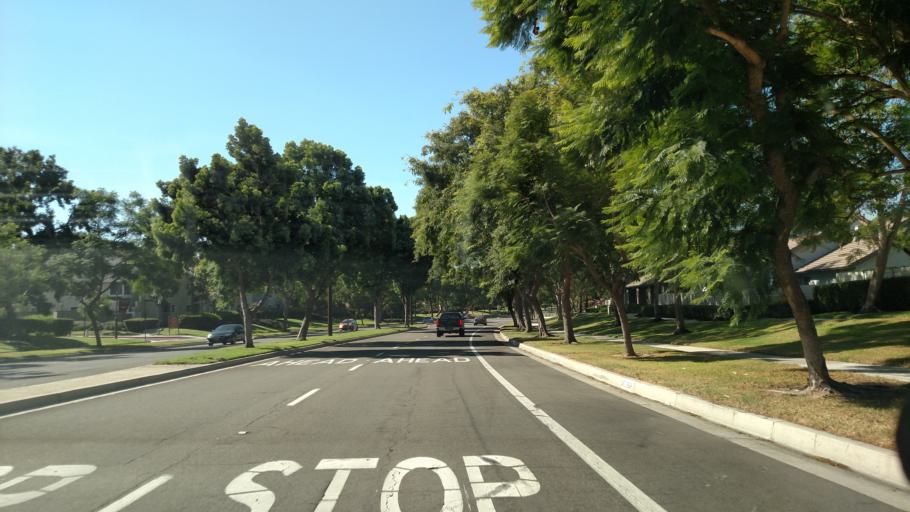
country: US
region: California
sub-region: Orange County
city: Irvine
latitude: 33.6698
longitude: -117.7924
